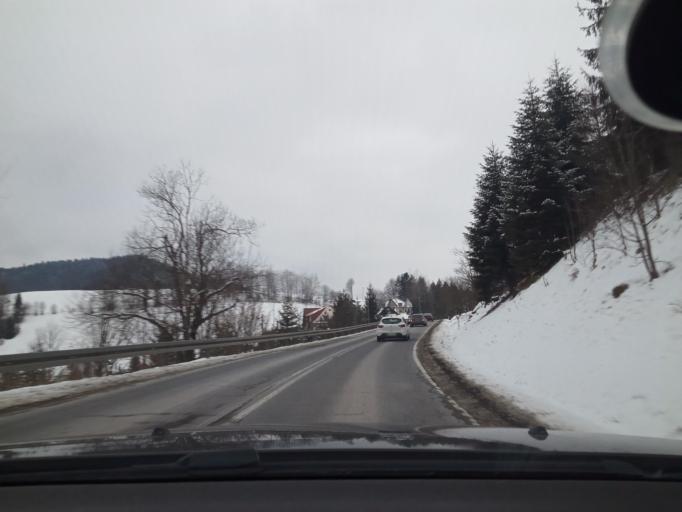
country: PL
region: Lesser Poland Voivodeship
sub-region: Powiat limanowski
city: Lubomierz
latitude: 49.5929
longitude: 20.2289
